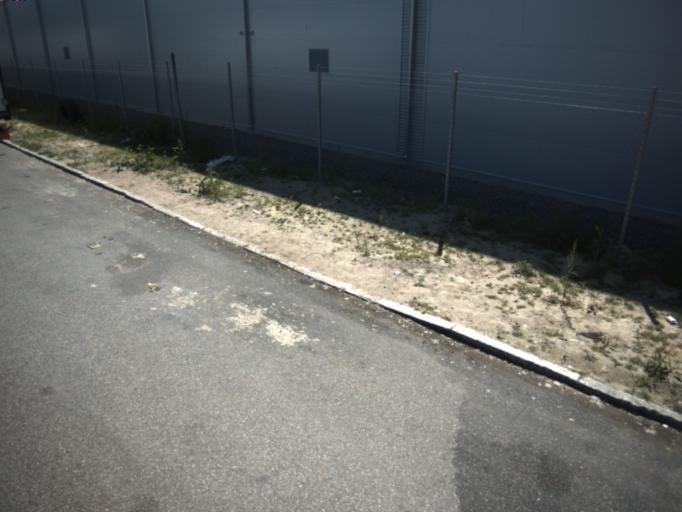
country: SE
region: Skane
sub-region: Helsingborg
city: Gantofta
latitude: 56.0153
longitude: 12.7693
